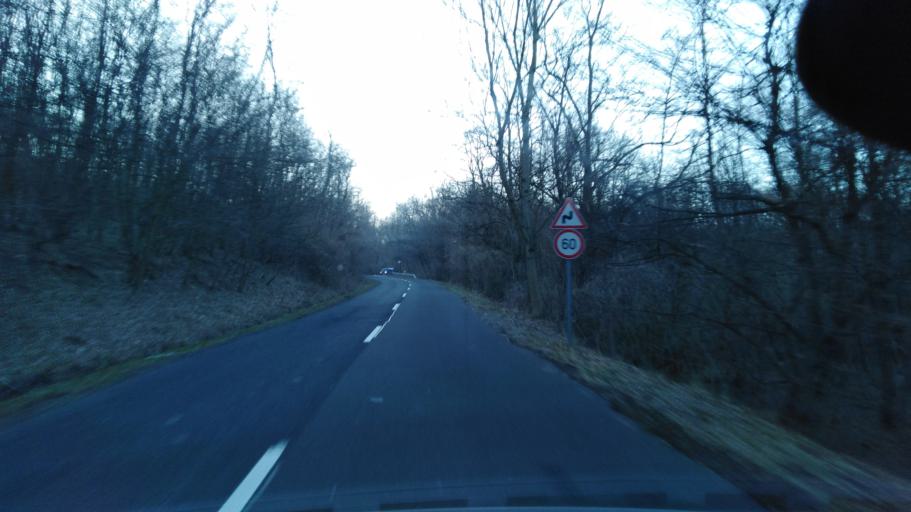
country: HU
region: Nograd
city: Salgotarjan
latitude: 48.0684
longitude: 19.8198
